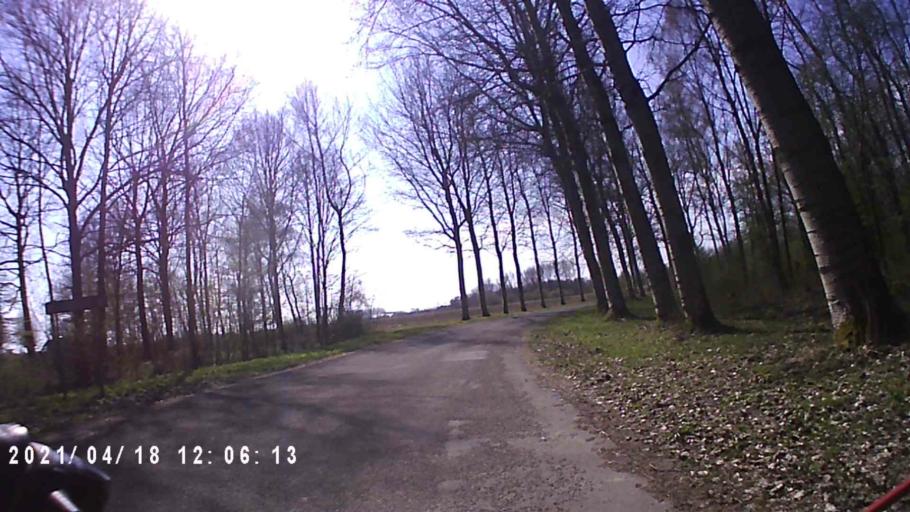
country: NL
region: Friesland
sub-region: Gemeente Kollumerland en Nieuwkruisland
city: Kollum
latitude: 53.3281
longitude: 6.1876
